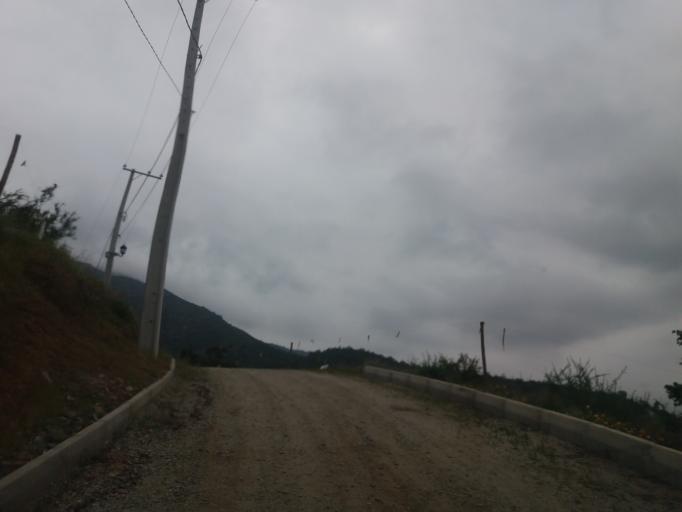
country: CL
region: Valparaiso
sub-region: Provincia de Marga Marga
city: Limache
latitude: -33.0240
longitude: -71.1320
